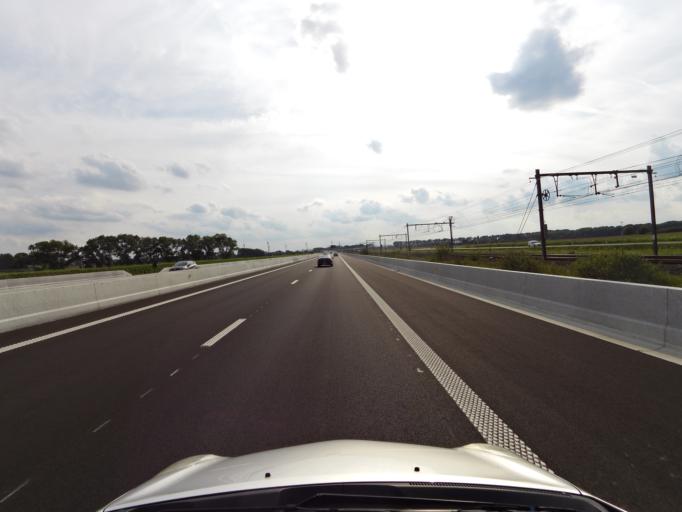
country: BE
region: Flanders
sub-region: Provincie West-Vlaanderen
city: Damme
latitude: 51.2834
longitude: 3.2292
